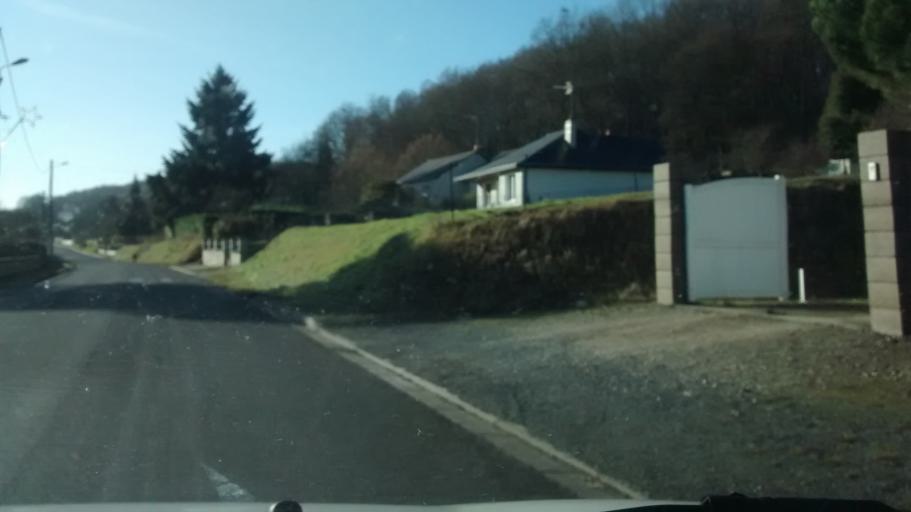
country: FR
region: Centre
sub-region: Departement d'Indre-et-Loire
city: Reugny
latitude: 47.4781
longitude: 0.8821
